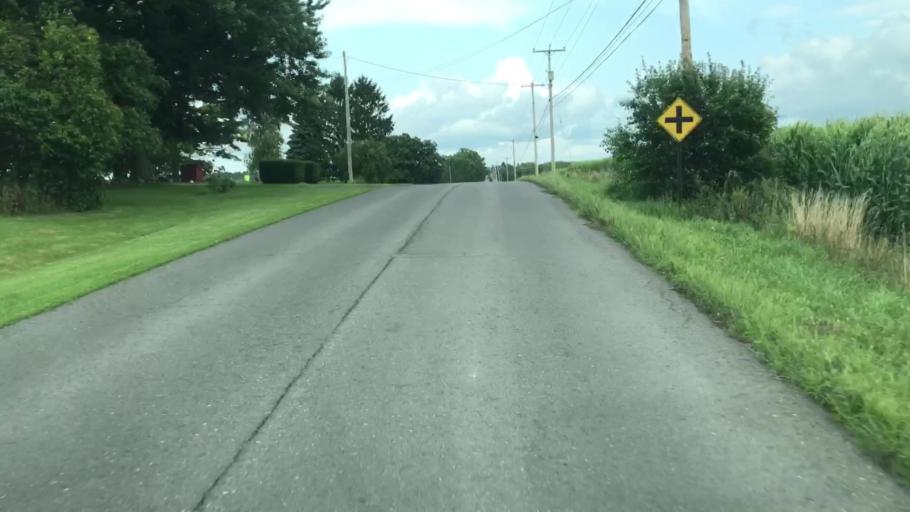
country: US
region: New York
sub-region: Onondaga County
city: Elbridge
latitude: 42.9853
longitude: -76.4967
